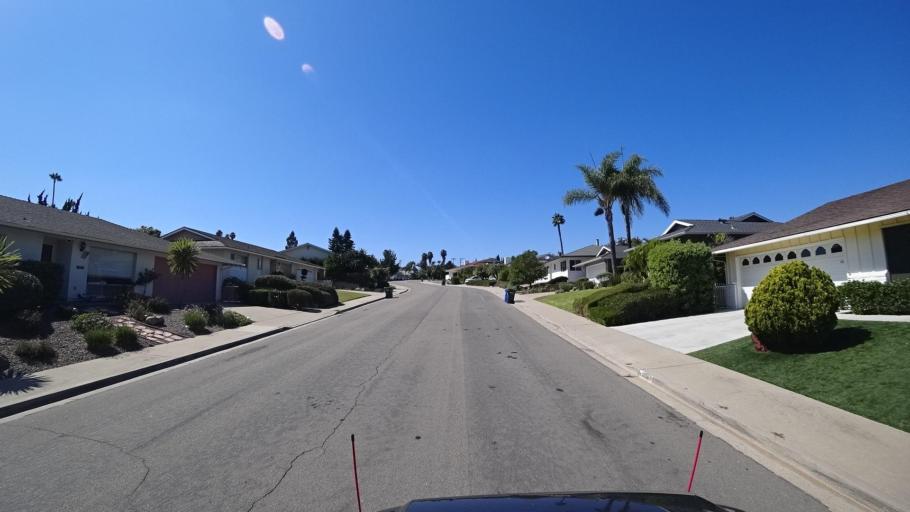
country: US
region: California
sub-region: San Diego County
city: Lake San Marcos
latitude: 33.1268
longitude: -117.2107
